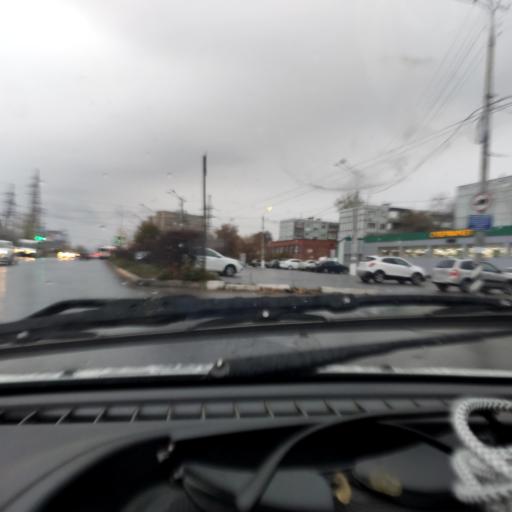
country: RU
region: Samara
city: Zhigulevsk
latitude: 53.4799
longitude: 49.5140
